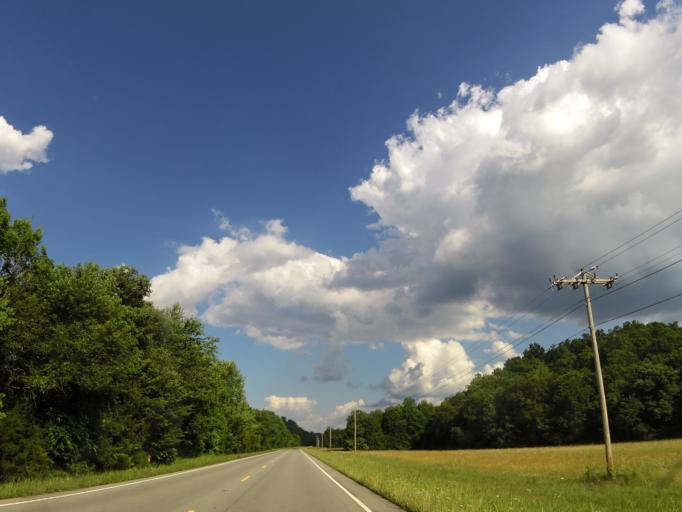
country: US
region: Tennessee
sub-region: Perry County
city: Linden
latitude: 35.6139
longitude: -87.7250
